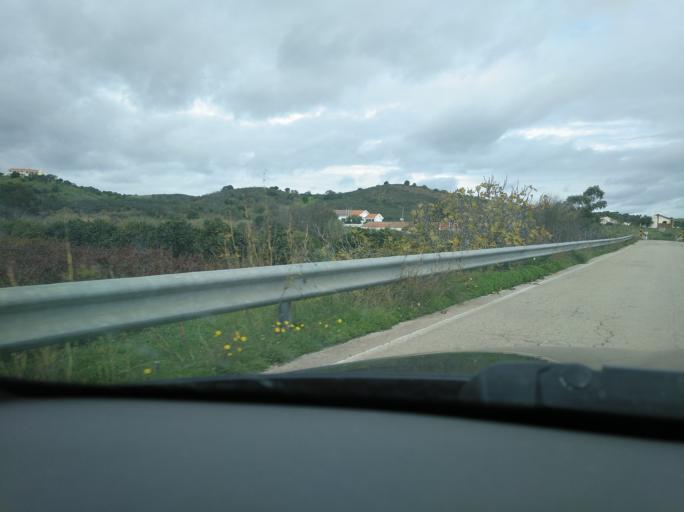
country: PT
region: Faro
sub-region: Castro Marim
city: Castro Marim
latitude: 37.2256
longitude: -7.4926
